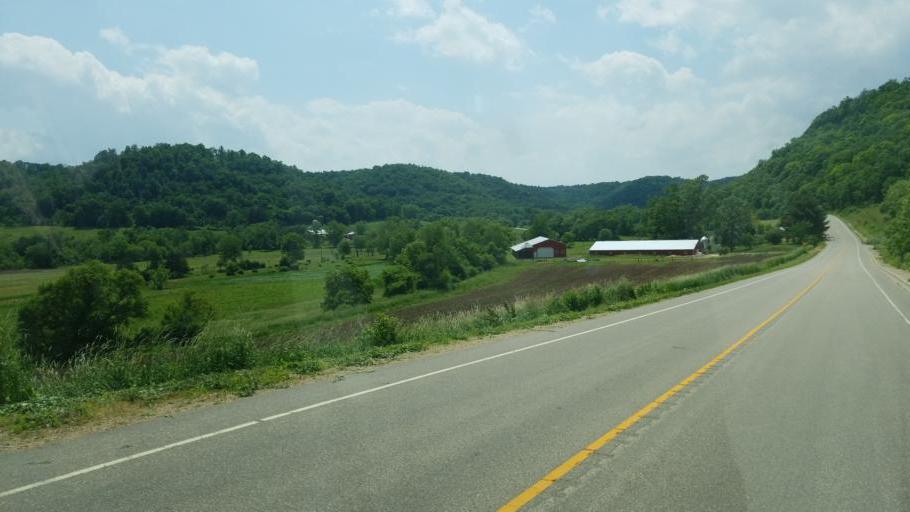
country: US
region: Wisconsin
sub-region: Vernon County
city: Viroqua
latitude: 43.4702
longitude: -90.7038
